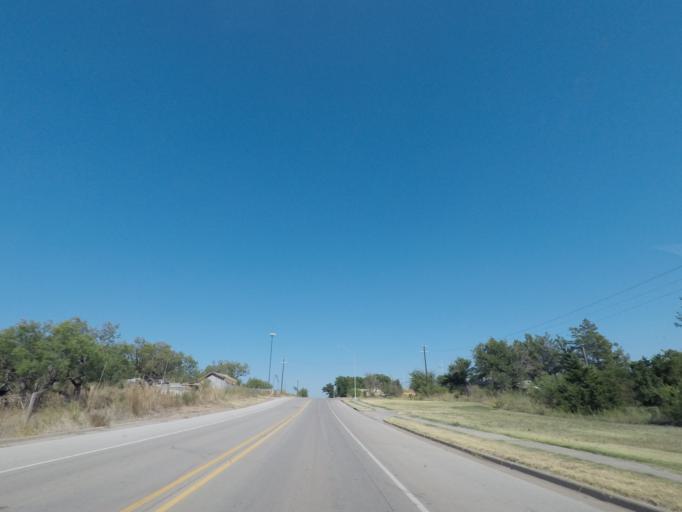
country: US
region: Texas
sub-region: Baylor County
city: Seymour
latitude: 33.5961
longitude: -99.2529
